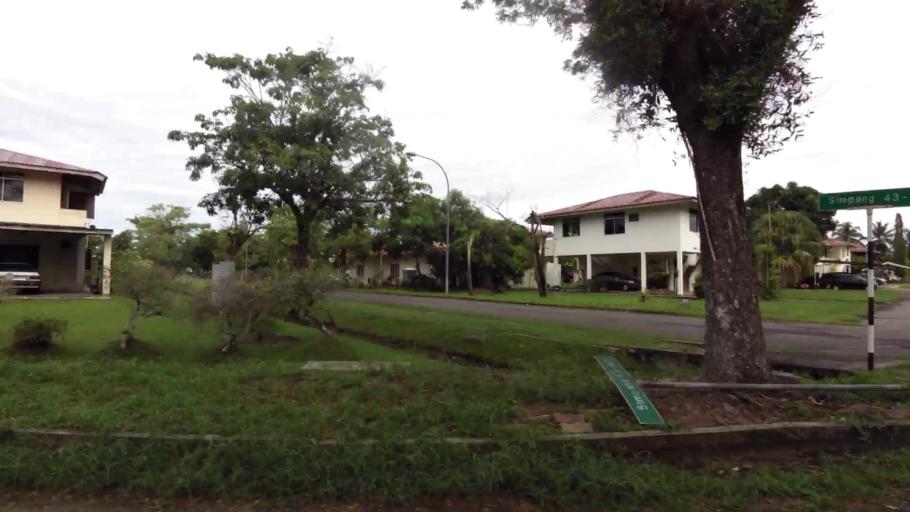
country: BN
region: Belait
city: Seria
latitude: 4.5971
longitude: 114.3274
